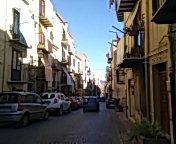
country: IT
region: Sicily
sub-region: Palermo
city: Castelbuono
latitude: 37.9294
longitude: 14.0897
